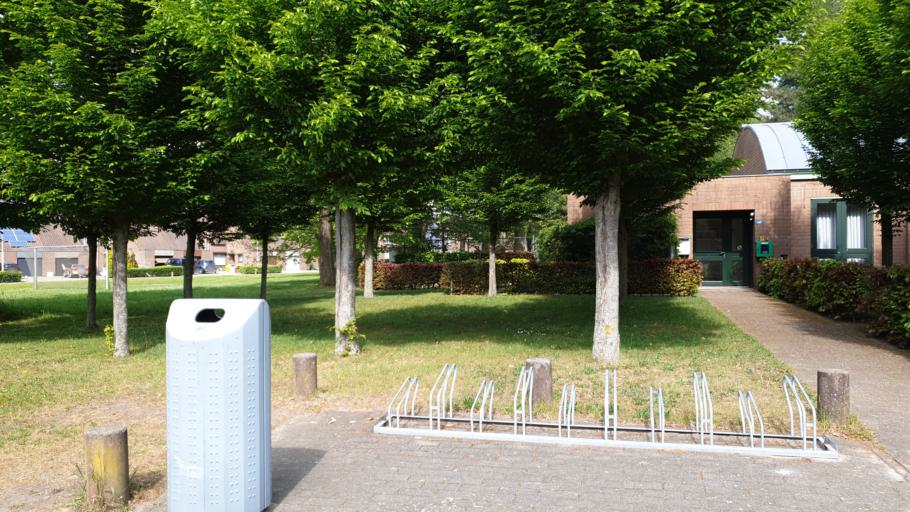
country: BE
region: Flanders
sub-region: Provincie Antwerpen
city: Herentals
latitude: 51.1804
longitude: 4.8576
